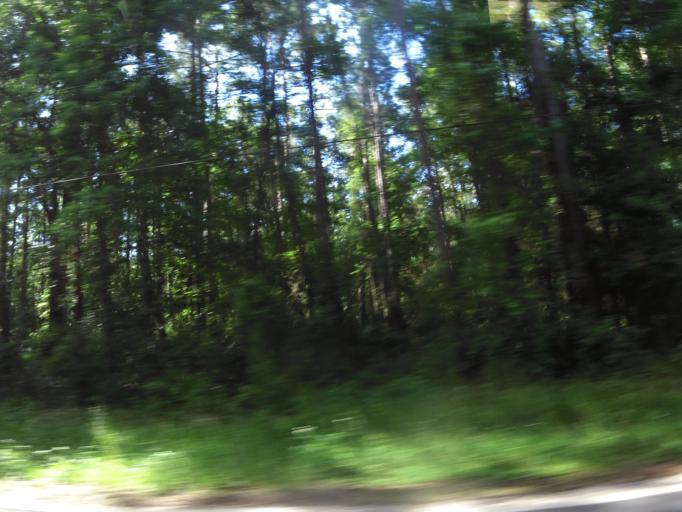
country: US
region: Florida
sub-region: Nassau County
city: Callahan
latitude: 30.5619
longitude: -81.8116
